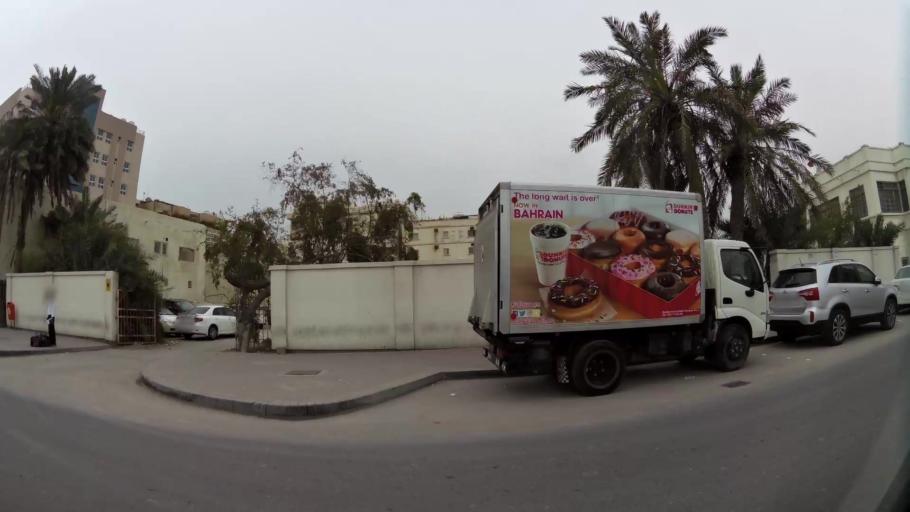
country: BH
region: Manama
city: Manama
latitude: 26.2315
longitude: 50.5714
